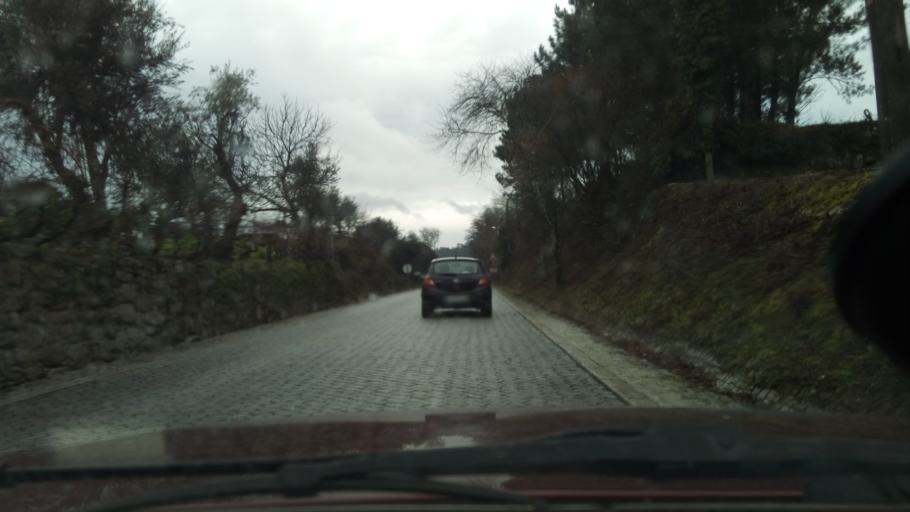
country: PT
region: Viseu
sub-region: Mangualde
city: Mangualde
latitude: 40.6085
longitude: -7.6534
